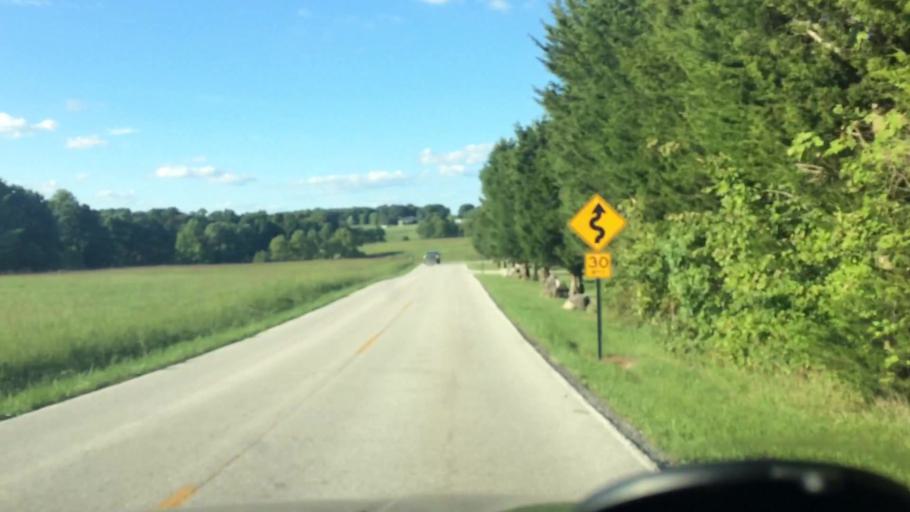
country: US
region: Missouri
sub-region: Greene County
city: Strafford
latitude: 37.2724
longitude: -93.0813
